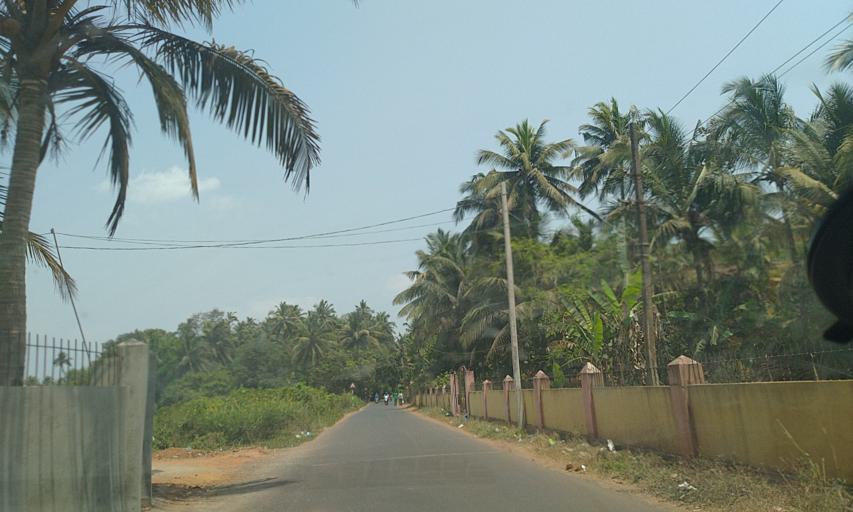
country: IN
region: Goa
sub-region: North Goa
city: Saligao
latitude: 15.5531
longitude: 73.8121
